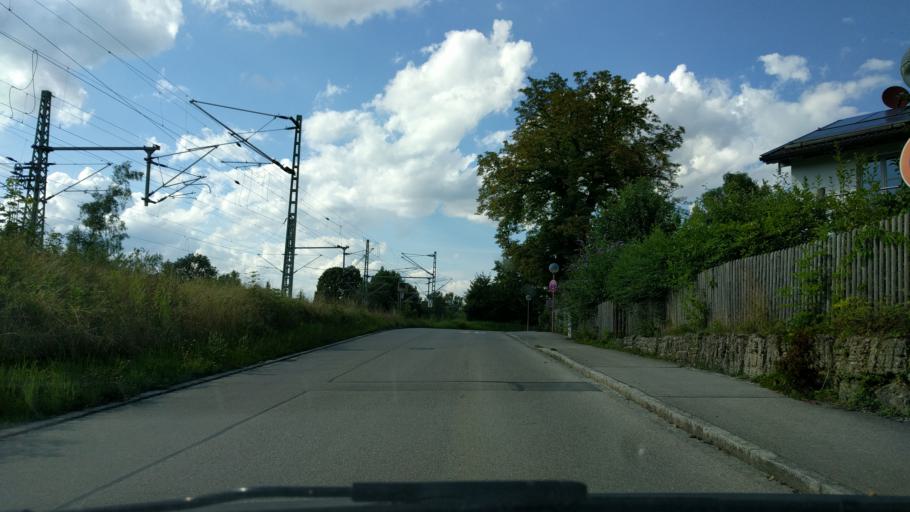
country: DE
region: Bavaria
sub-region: Upper Bavaria
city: Oberhaching
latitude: 48.0220
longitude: 11.5827
